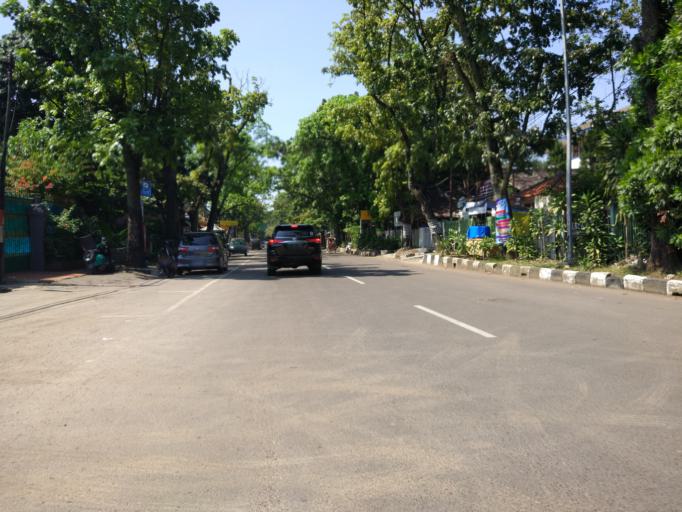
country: ID
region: West Java
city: Bandung
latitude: -6.9300
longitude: 107.6203
